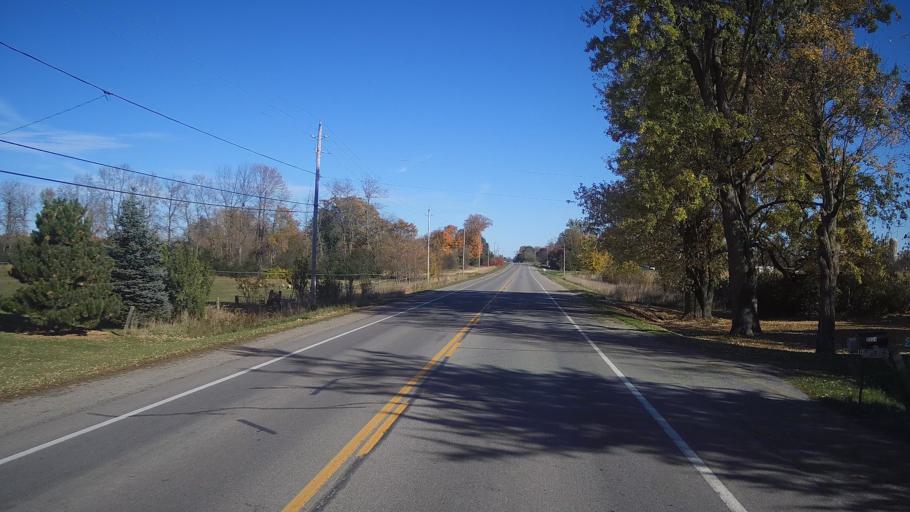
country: CA
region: Ontario
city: Kingston
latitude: 44.4073
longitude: -76.5559
